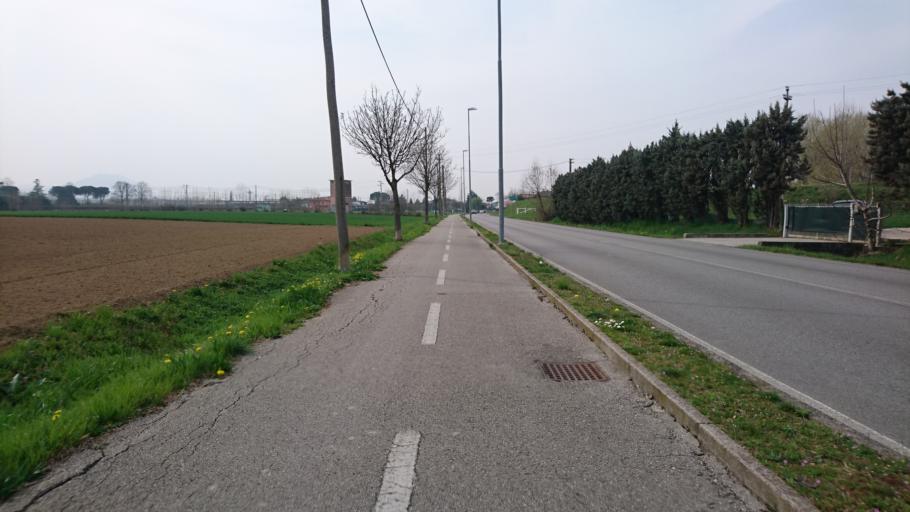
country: IT
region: Veneto
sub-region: Provincia di Padova
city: Selvazzano Dentro
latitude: 45.3937
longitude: 11.7735
